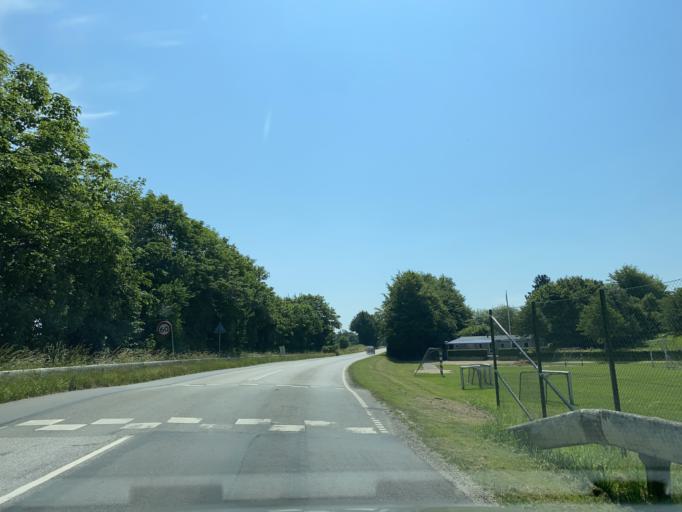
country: DK
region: South Denmark
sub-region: Sonderborg Kommune
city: Grasten
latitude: 55.0130
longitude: 9.5707
